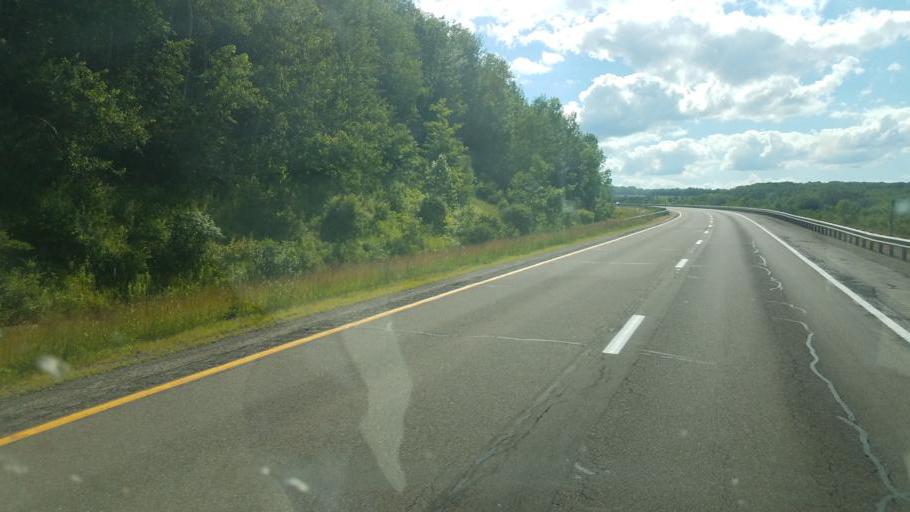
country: US
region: New York
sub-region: Allegany County
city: Alfred
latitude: 42.3171
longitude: -77.8486
